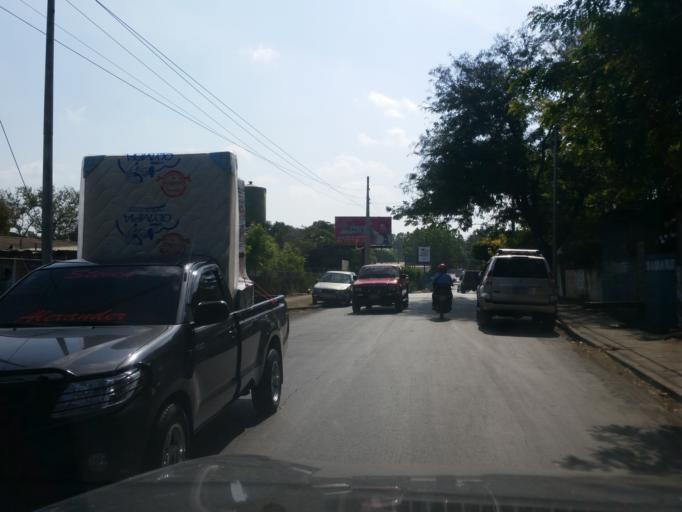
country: NI
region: Managua
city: Managua
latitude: 12.1234
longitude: -86.2124
